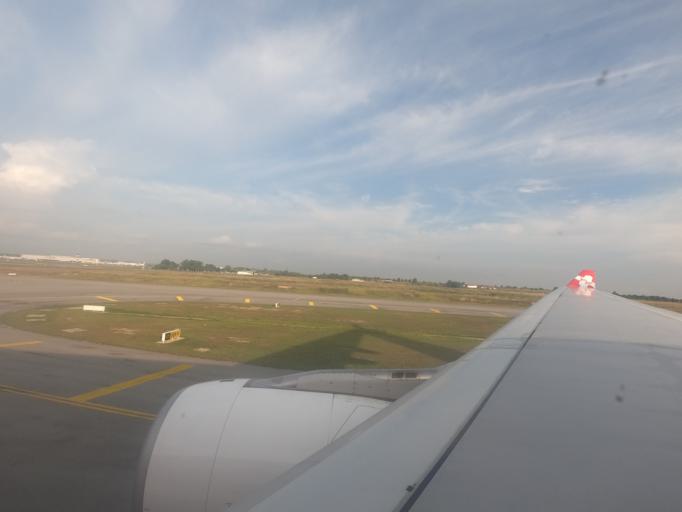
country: MY
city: Sungai Pelek New Village
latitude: 2.7404
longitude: 101.6932
